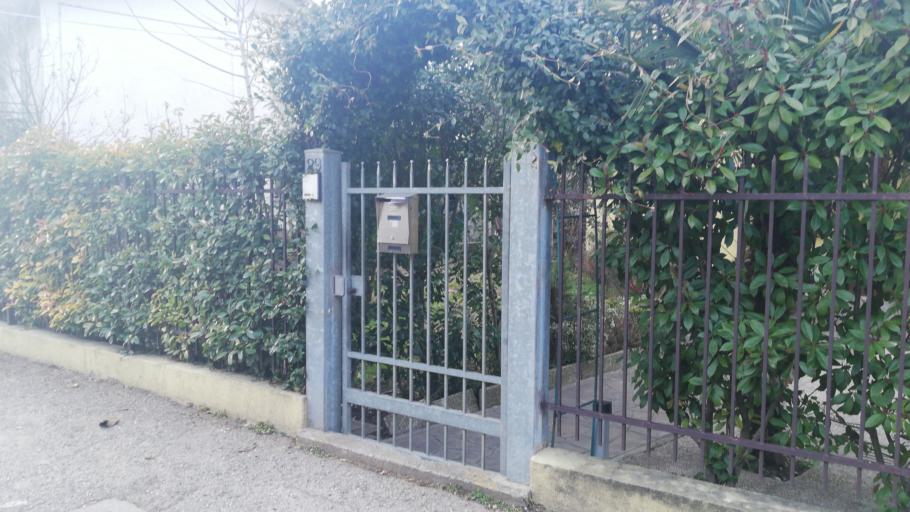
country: IT
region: Veneto
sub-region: Provincia di Venezia
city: Campalto
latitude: 45.4837
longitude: 12.2904
